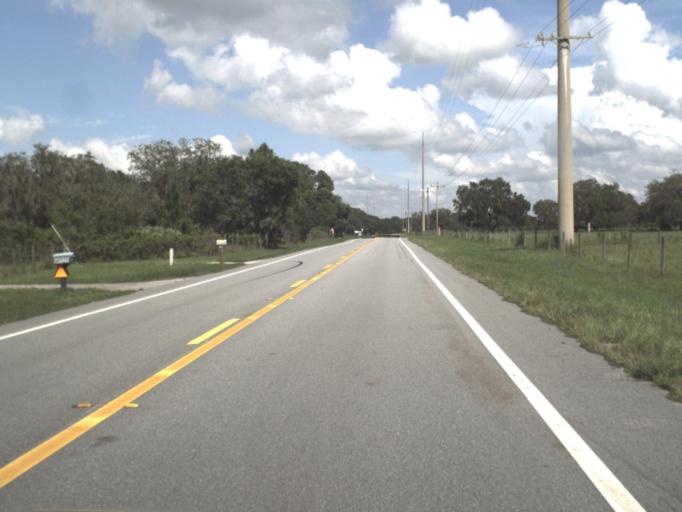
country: US
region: Florida
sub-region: Hardee County
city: Wauchula
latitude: 27.4655
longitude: -82.0795
